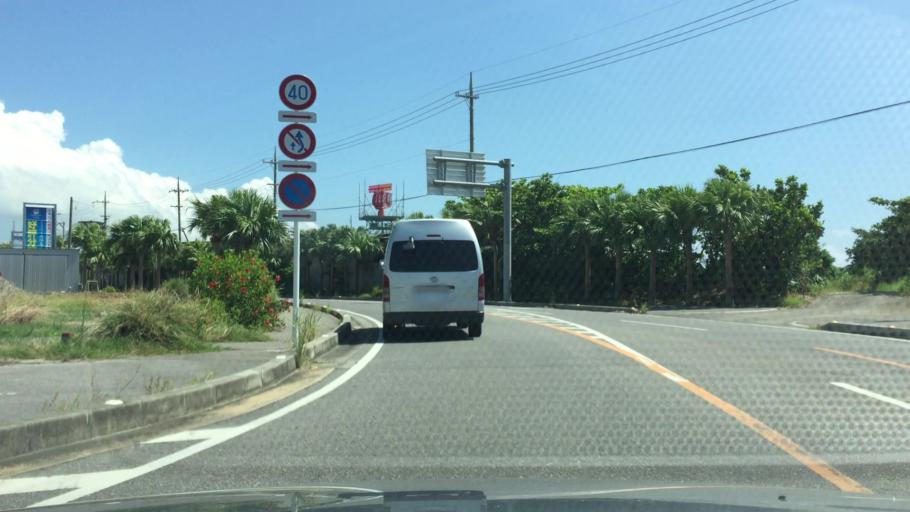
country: JP
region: Okinawa
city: Ishigaki
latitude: 24.3846
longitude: 124.2440
